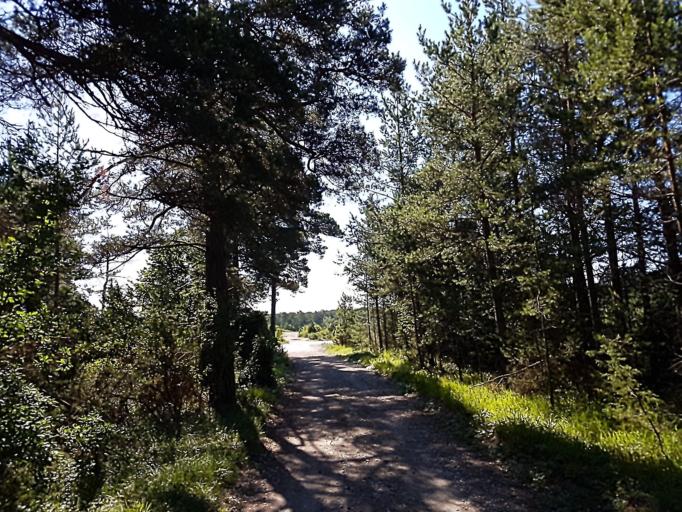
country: SE
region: Gotland
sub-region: Gotland
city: Visby
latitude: 57.6109
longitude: 18.3643
